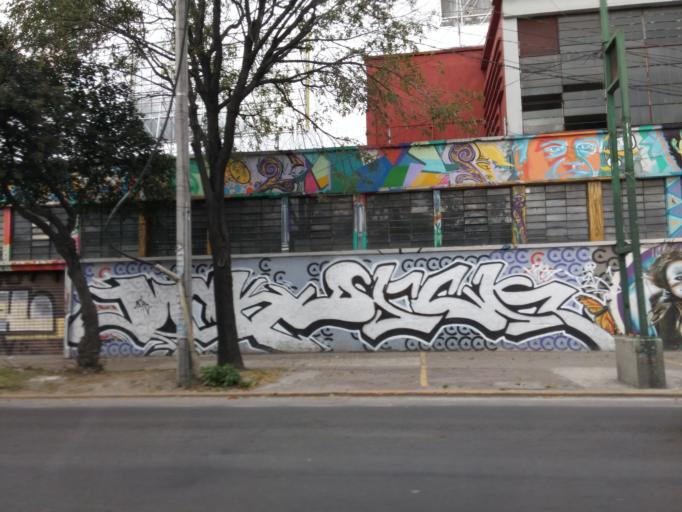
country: MX
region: Mexico City
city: Cuauhtemoc
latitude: 19.4596
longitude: -99.1618
